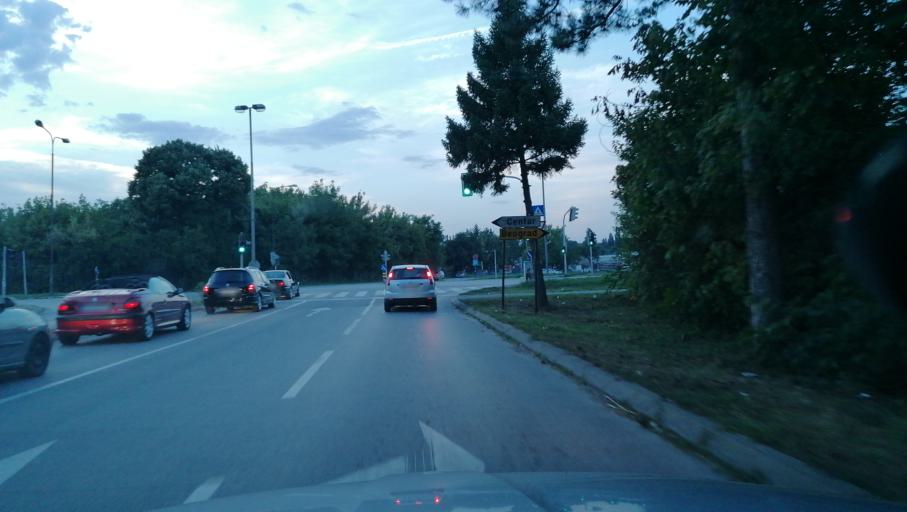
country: RS
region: Central Serbia
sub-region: Kolubarski Okrug
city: Valjevo
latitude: 44.2743
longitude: 19.9081
